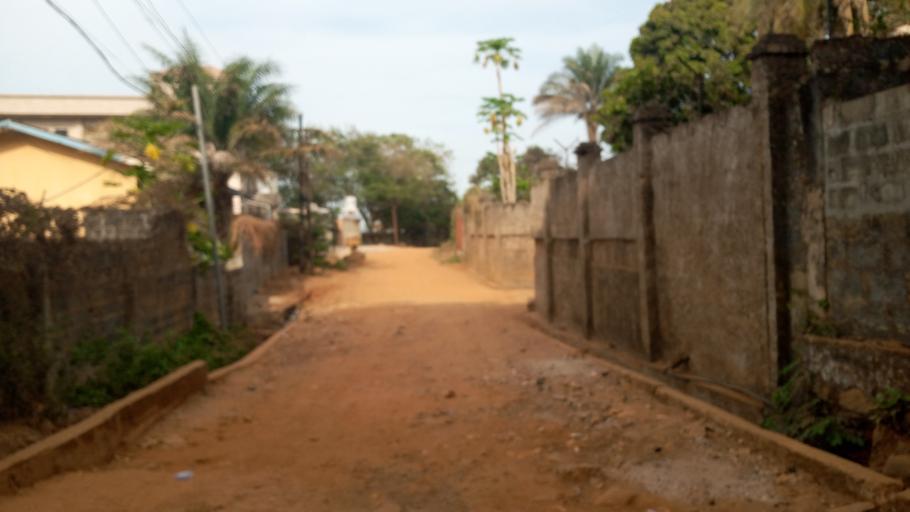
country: SL
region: Western Area
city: Freetown
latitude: 8.4815
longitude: -13.2638
